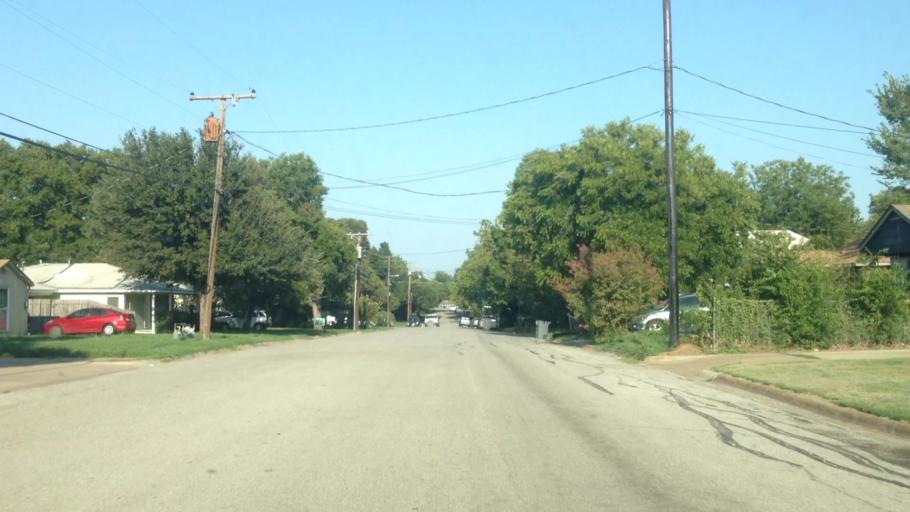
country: US
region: Texas
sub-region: Tarrant County
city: Haltom City
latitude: 32.8000
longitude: -97.2617
